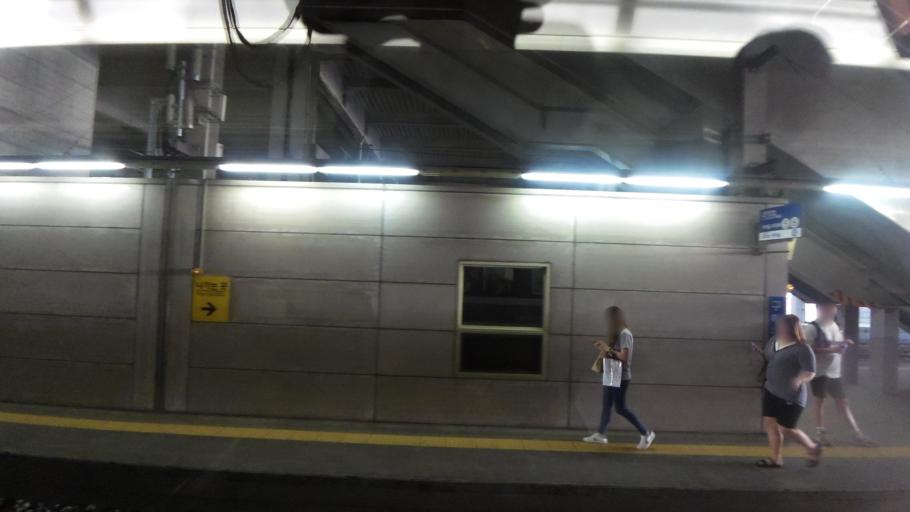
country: KR
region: Gyeongsangbuk-do
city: Gumi
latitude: 36.1282
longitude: 128.3308
